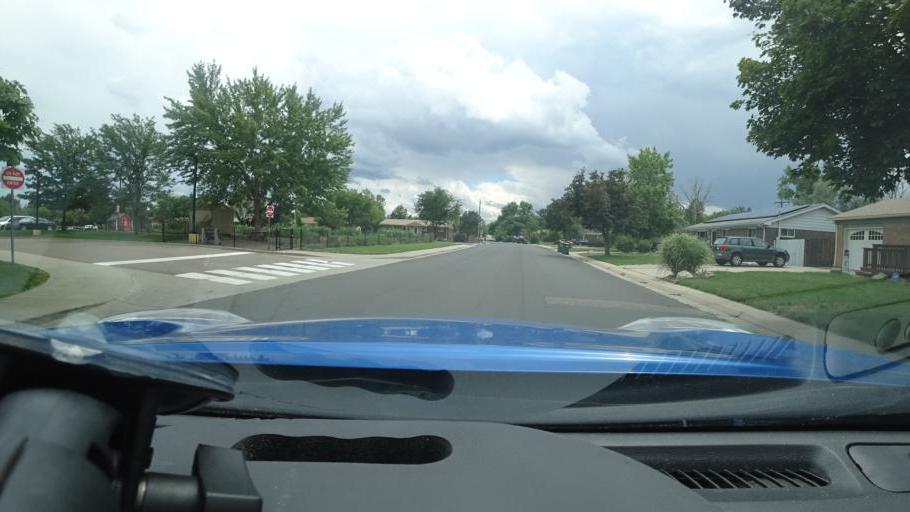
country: US
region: Colorado
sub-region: Adams County
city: Aurora
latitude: 39.7241
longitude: -104.8312
